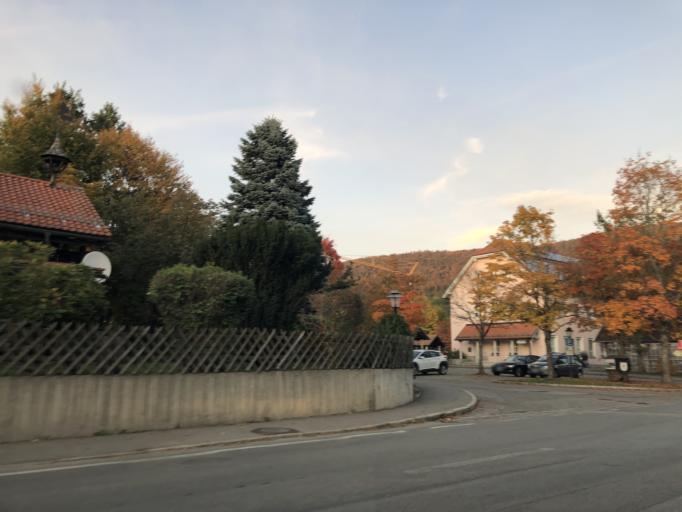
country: DE
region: Bavaria
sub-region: Lower Bavaria
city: Bodenmais
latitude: 49.0698
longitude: 13.1008
